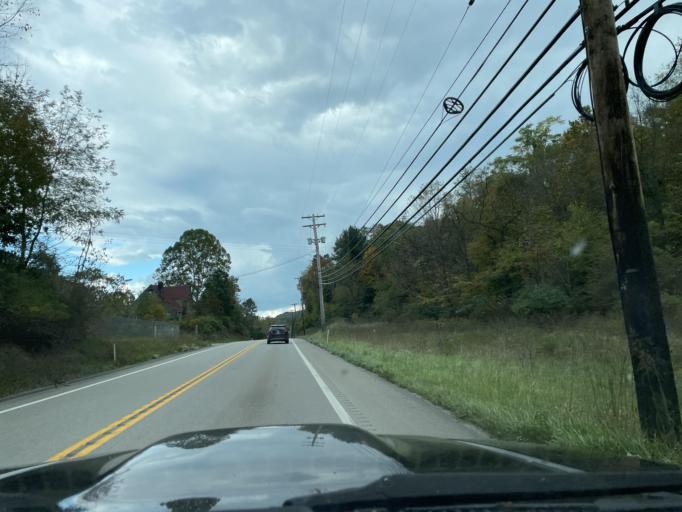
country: US
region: Pennsylvania
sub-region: Westmoreland County
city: Lower Burrell
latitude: 40.5406
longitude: -79.7224
